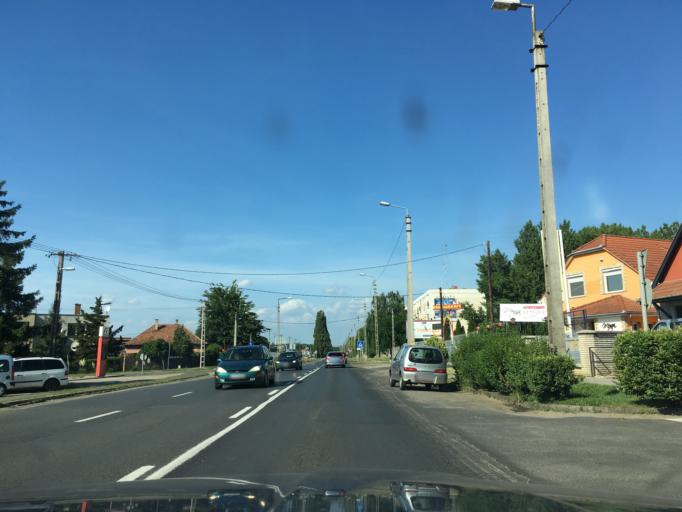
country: HU
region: Hajdu-Bihar
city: Debrecen
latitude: 47.5526
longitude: 21.6646
